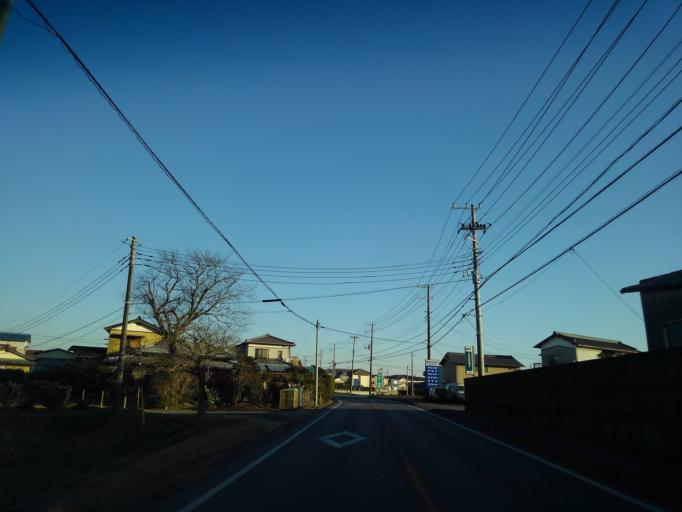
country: JP
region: Chiba
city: Kimitsu
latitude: 35.3095
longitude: 139.9391
